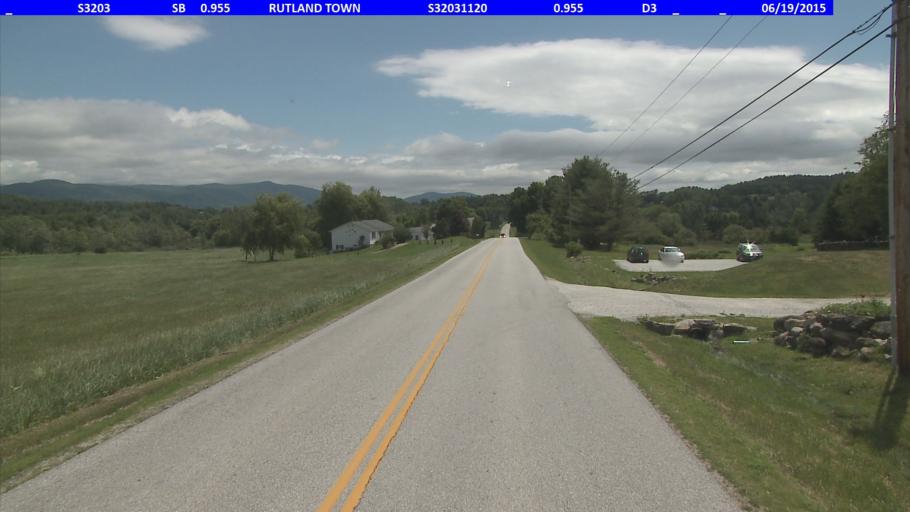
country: US
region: Vermont
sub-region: Rutland County
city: Rutland
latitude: 43.6662
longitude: -73.0026
